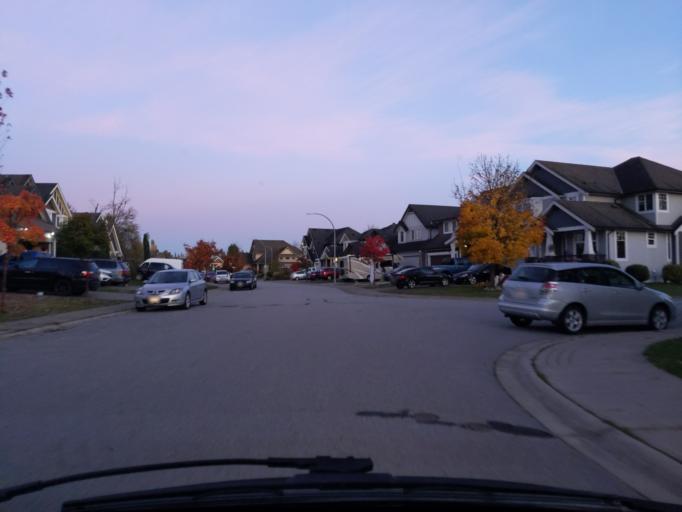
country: CA
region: British Columbia
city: Walnut Grove
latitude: 49.1827
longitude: -122.6589
